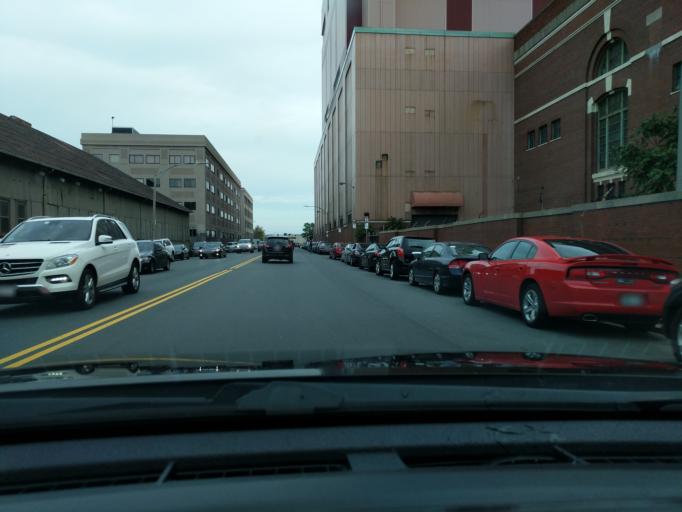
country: US
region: Massachusetts
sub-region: Suffolk County
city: South Boston
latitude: 42.3385
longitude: -71.0355
